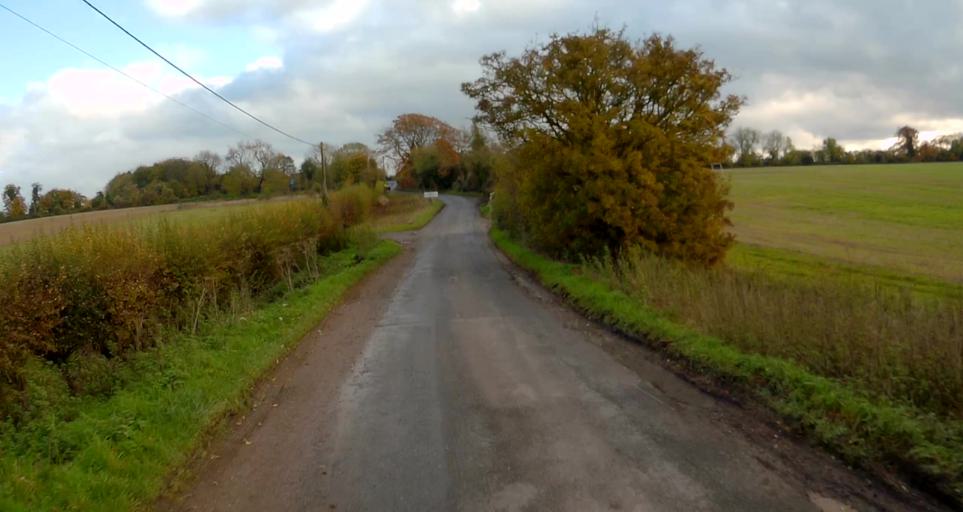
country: GB
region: England
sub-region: Hampshire
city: Long Sutton
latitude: 51.2236
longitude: -0.9790
